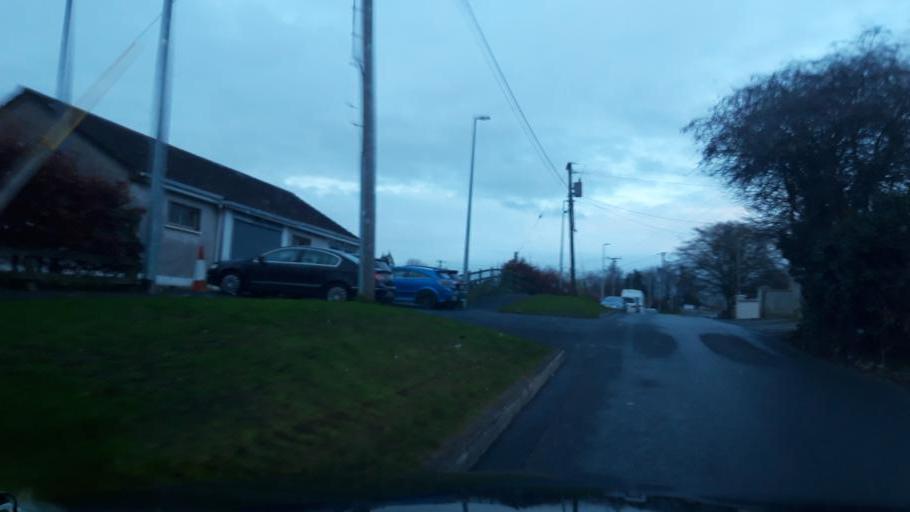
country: IE
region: Leinster
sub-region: Kilkenny
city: Kilkenny
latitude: 52.6643
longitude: -7.2429
